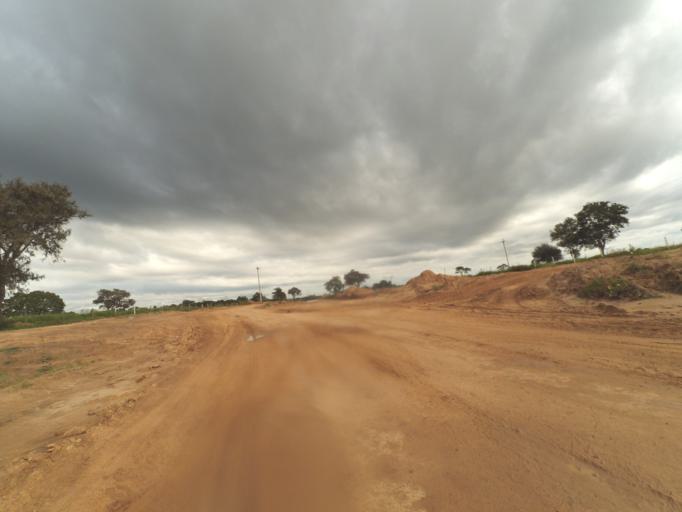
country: BO
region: Santa Cruz
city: Santa Cruz de la Sierra
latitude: -17.7124
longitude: -63.2792
